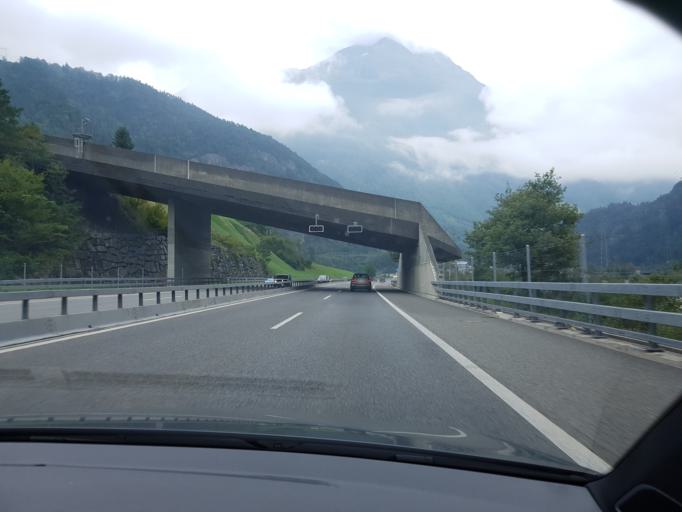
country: CH
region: Uri
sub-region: Uri
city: Silenen
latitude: 46.7847
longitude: 8.6685
